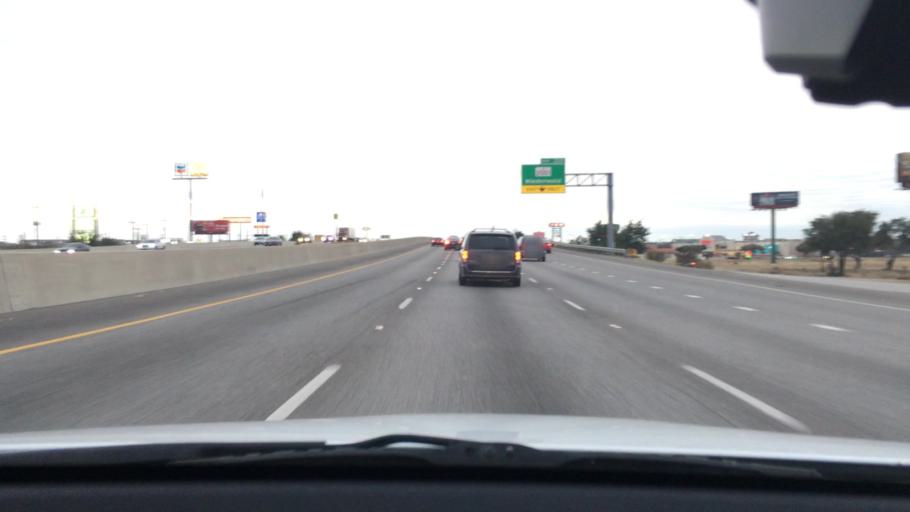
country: US
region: Texas
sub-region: Hays County
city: Buda
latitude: 30.0915
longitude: -97.8174
